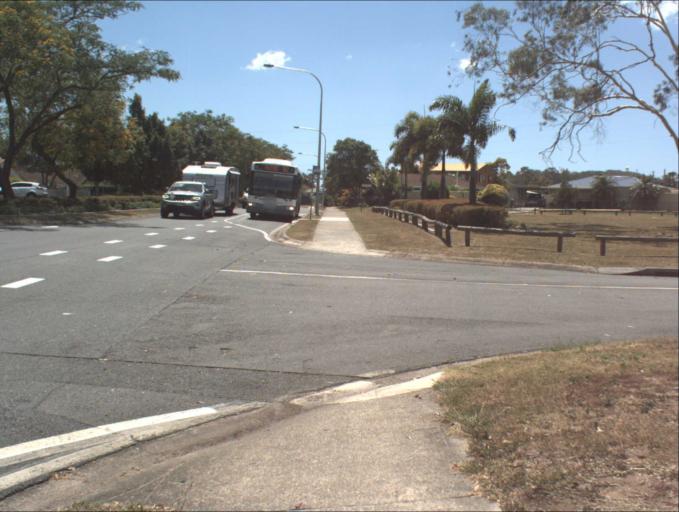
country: AU
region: Queensland
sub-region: Gold Coast
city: Yatala
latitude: -27.7267
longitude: 153.2109
